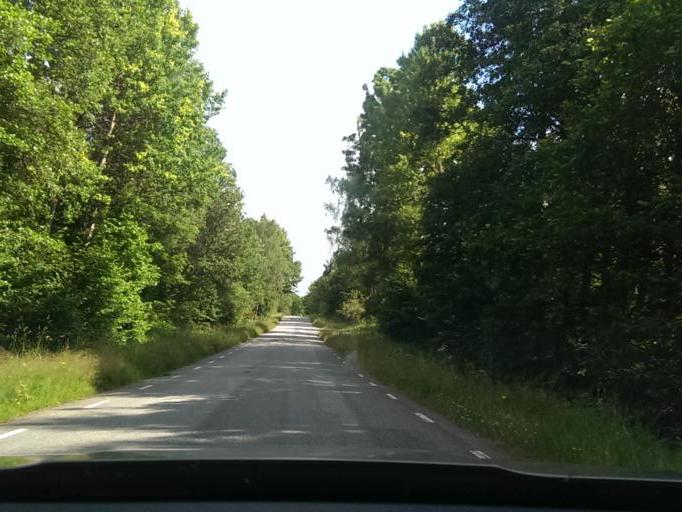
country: SE
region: Joenkoeping
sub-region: Varnamo Kommun
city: Forsheda
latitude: 57.0929
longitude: 13.8702
